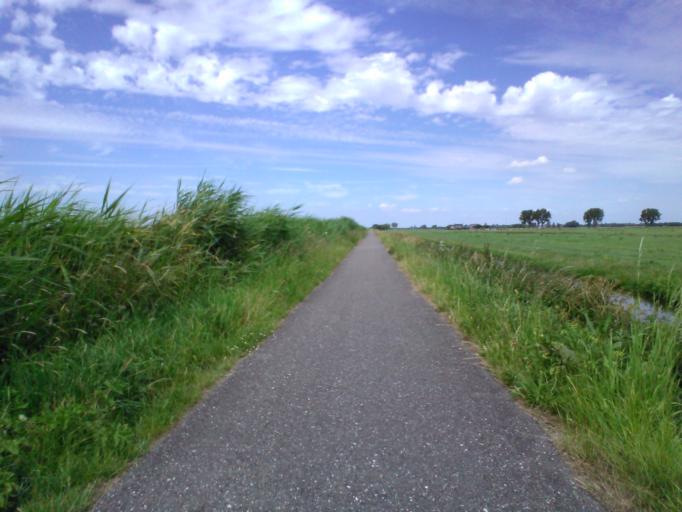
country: NL
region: South Holland
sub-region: Gemeente Giessenlanden
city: Giessenburg
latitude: 51.8559
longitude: 4.8848
